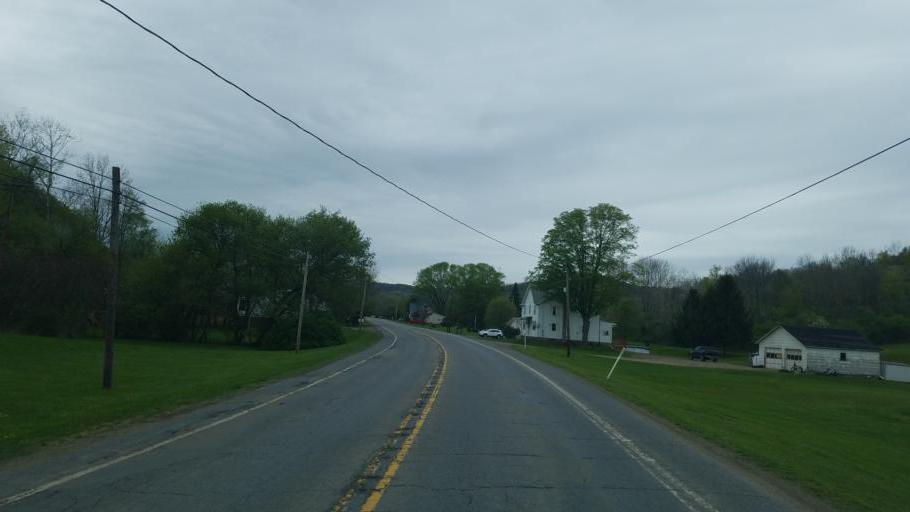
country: US
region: Pennsylvania
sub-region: Tioga County
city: Westfield
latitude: 41.9307
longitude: -77.6293
